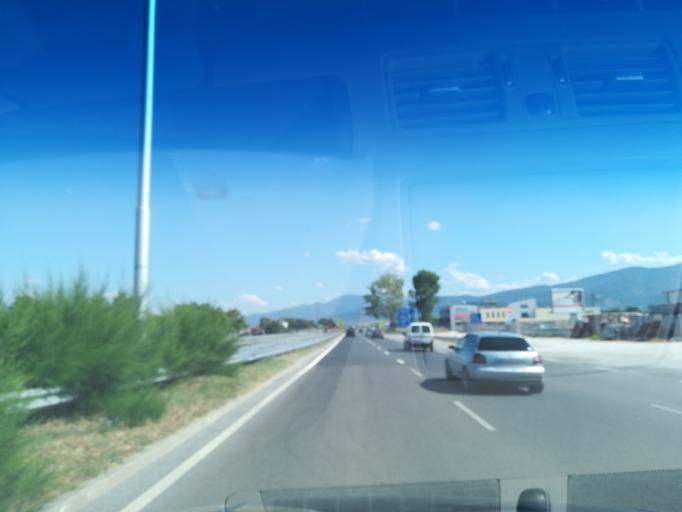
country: BG
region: Plovdiv
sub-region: Obshtina Plovdiv
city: Plovdiv
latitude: 42.1020
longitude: 24.7863
